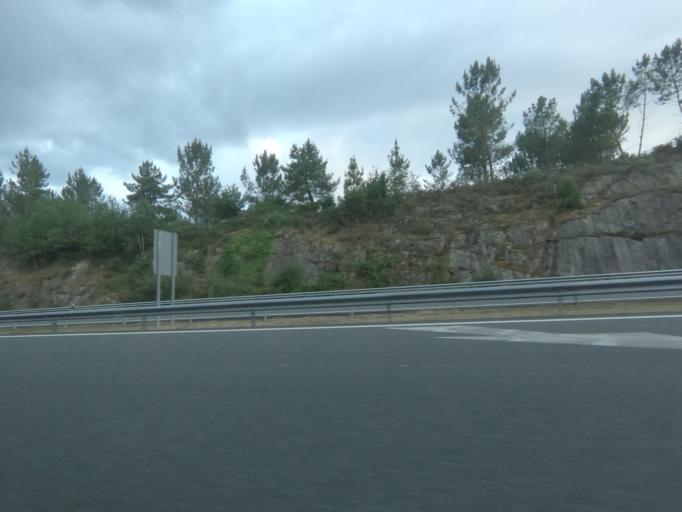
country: ES
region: Galicia
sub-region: Provincia de Ourense
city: Carballeda de Avia
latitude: 42.3072
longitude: -8.1571
